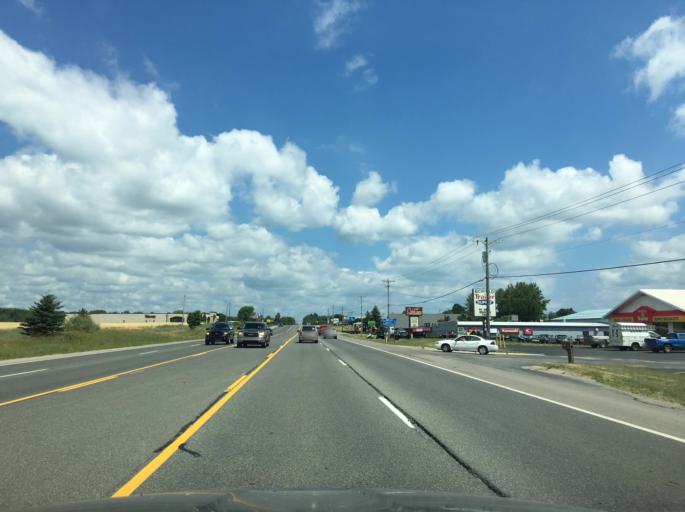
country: US
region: Michigan
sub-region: Grand Traverse County
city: Traverse City
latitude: 44.6928
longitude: -85.6562
